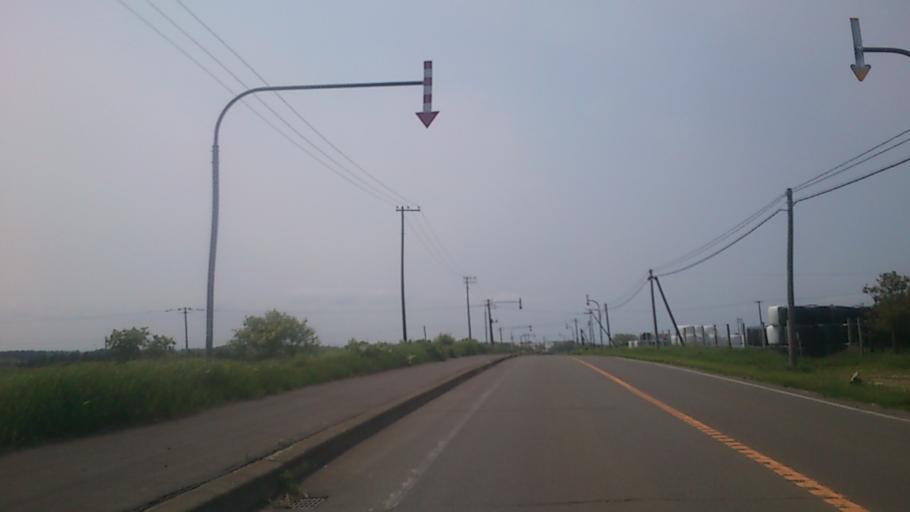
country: JP
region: Hokkaido
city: Nemuro
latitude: 43.2735
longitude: 145.5313
